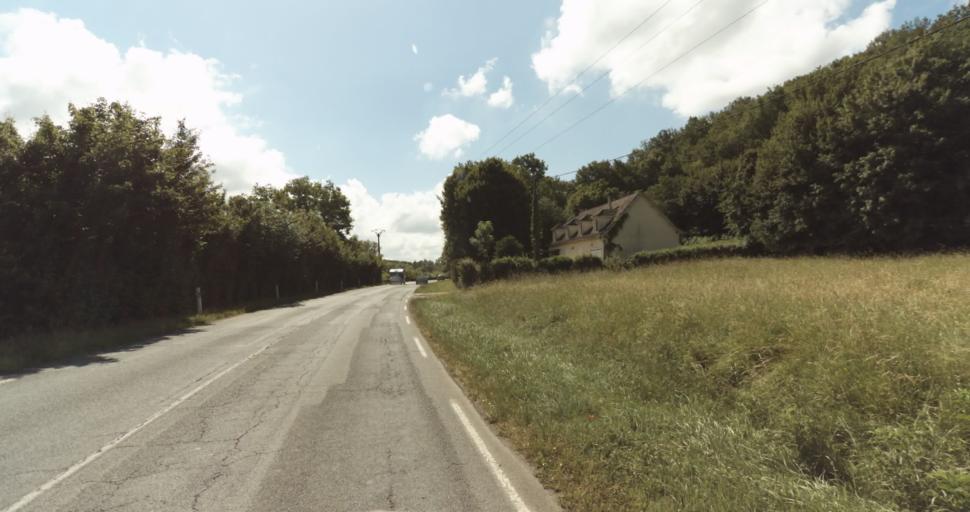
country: FR
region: Aquitaine
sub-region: Departement de la Dordogne
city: Le Bugue
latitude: 44.8421
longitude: 0.9294
